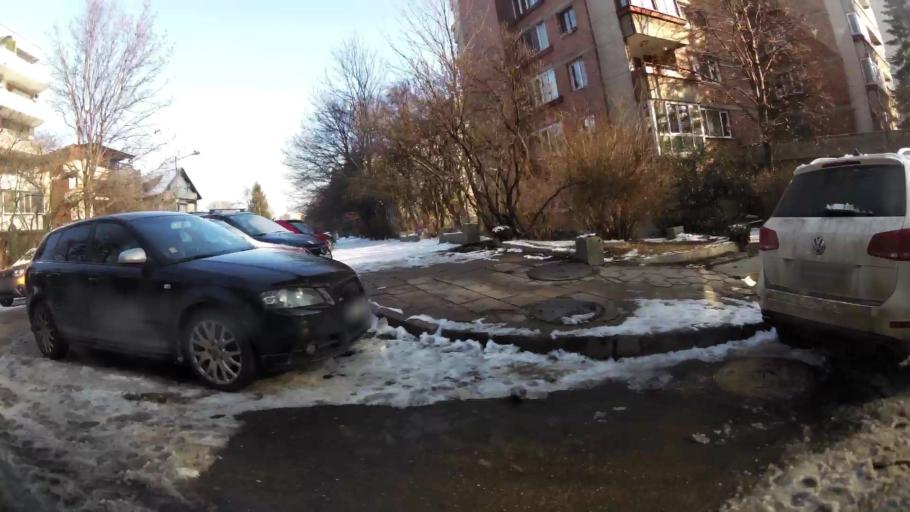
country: BG
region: Sofia-Capital
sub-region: Stolichna Obshtina
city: Sofia
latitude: 42.6694
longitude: 23.3440
